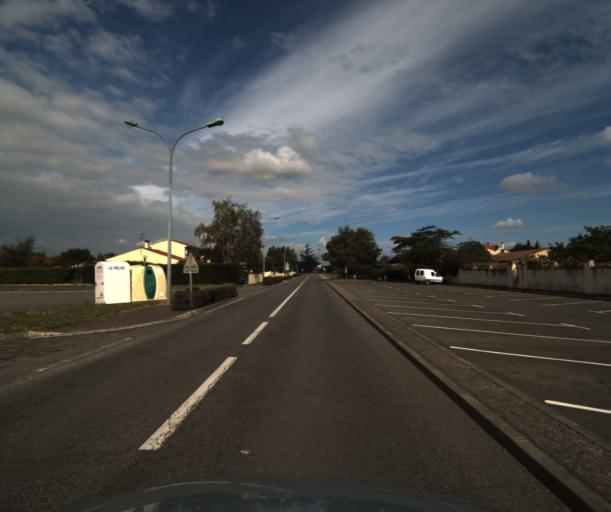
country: FR
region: Midi-Pyrenees
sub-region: Departement de la Haute-Garonne
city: Muret
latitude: 43.4692
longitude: 1.3207
